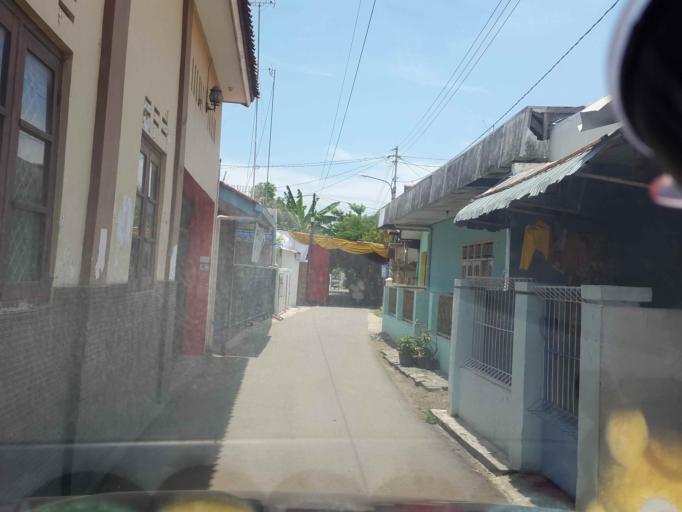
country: ID
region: Central Java
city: Tegal
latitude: -6.8650
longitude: 109.1389
